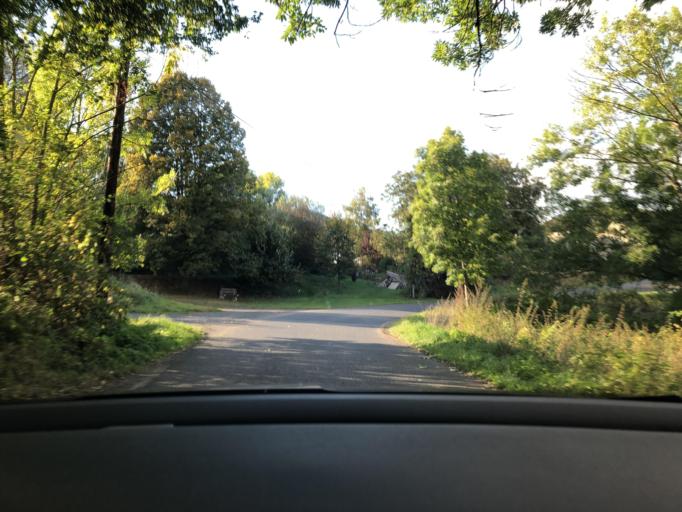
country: CZ
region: Ustecky
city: Zitenice
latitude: 50.5716
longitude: 14.1838
